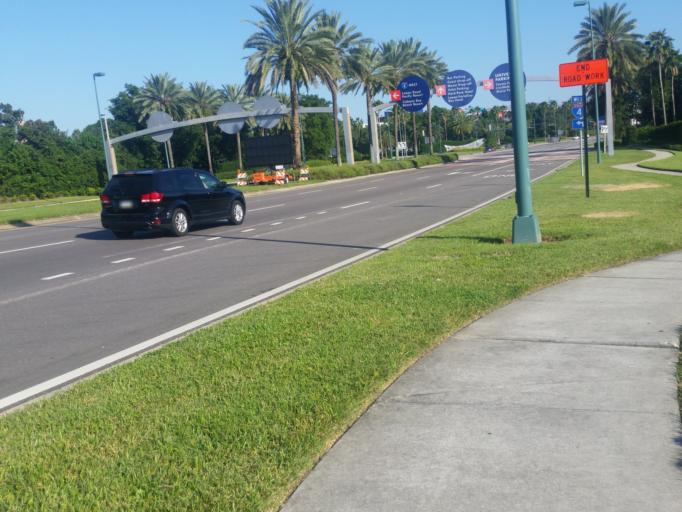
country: US
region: Florida
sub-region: Orange County
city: Tangelo Park
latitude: 28.4690
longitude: -81.4647
